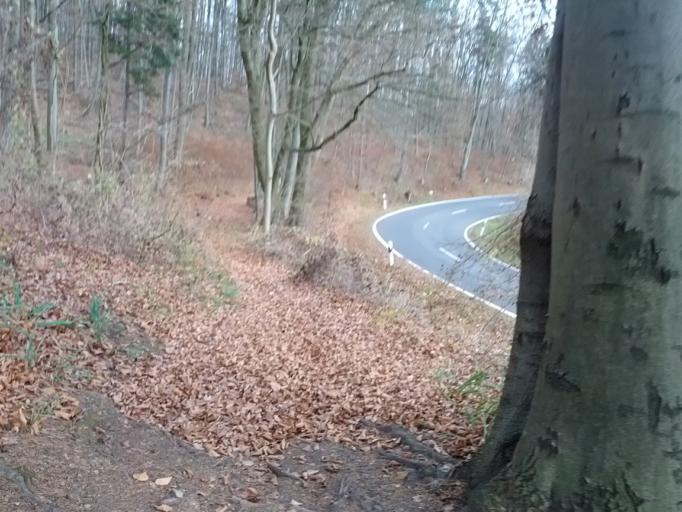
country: DE
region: Thuringia
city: Wolfsburg-Unkeroda
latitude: 50.9538
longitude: 10.2500
